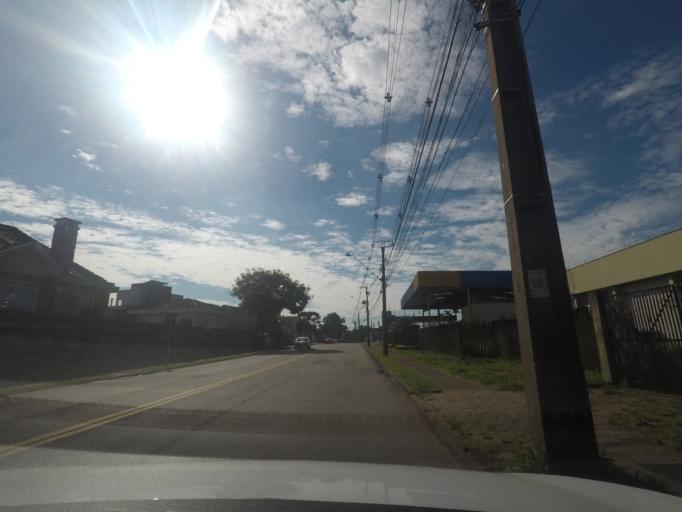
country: BR
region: Parana
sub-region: Curitiba
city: Curitiba
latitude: -25.4953
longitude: -49.2673
